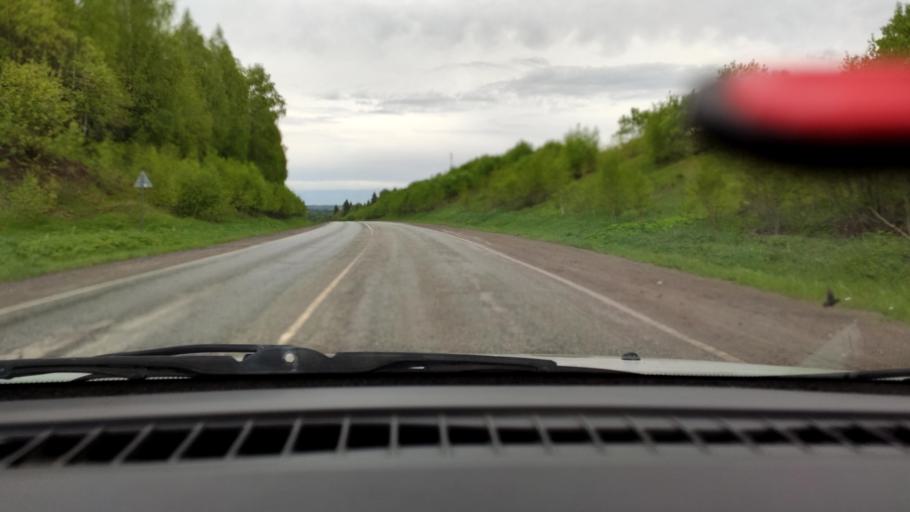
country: RU
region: Perm
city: Bershet'
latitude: 57.7503
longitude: 56.3692
